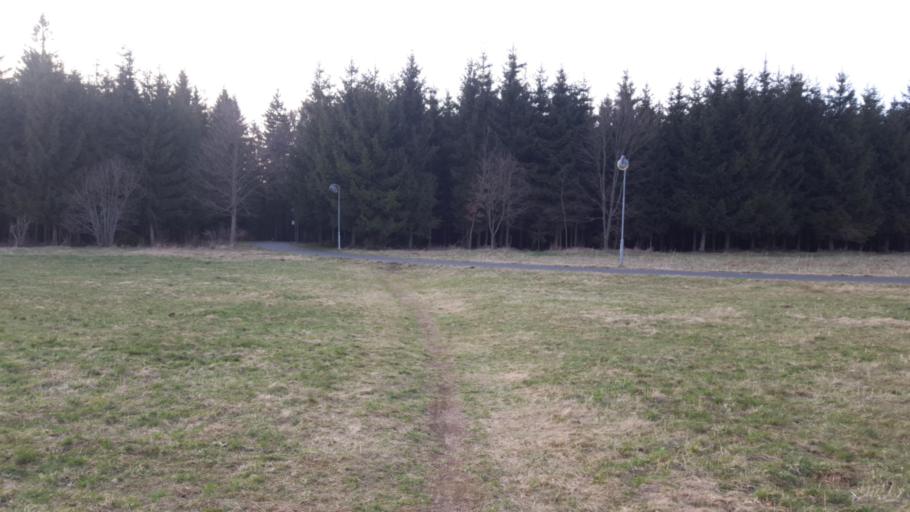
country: CZ
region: Karlovarsky
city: As
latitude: 50.2283
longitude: 12.2025
